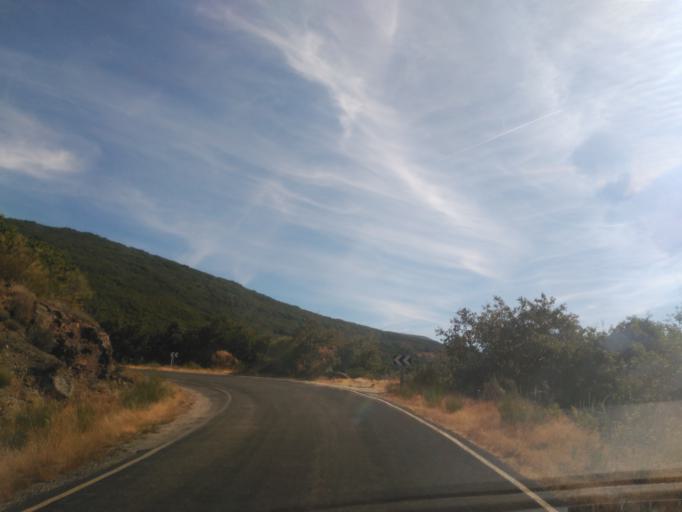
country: ES
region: Castille and Leon
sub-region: Provincia de Zamora
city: Cobreros
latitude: 42.1400
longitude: -6.7273
